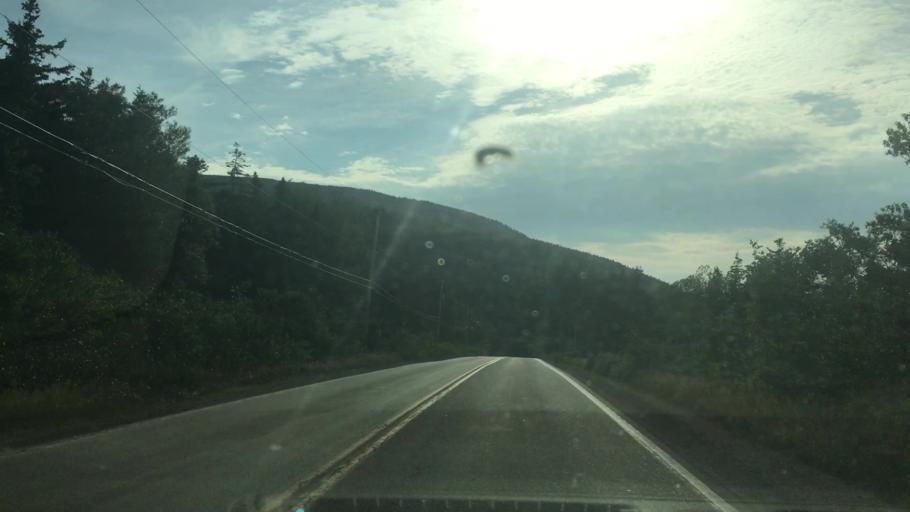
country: CA
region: Nova Scotia
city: Sydney Mines
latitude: 46.8236
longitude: -60.8226
